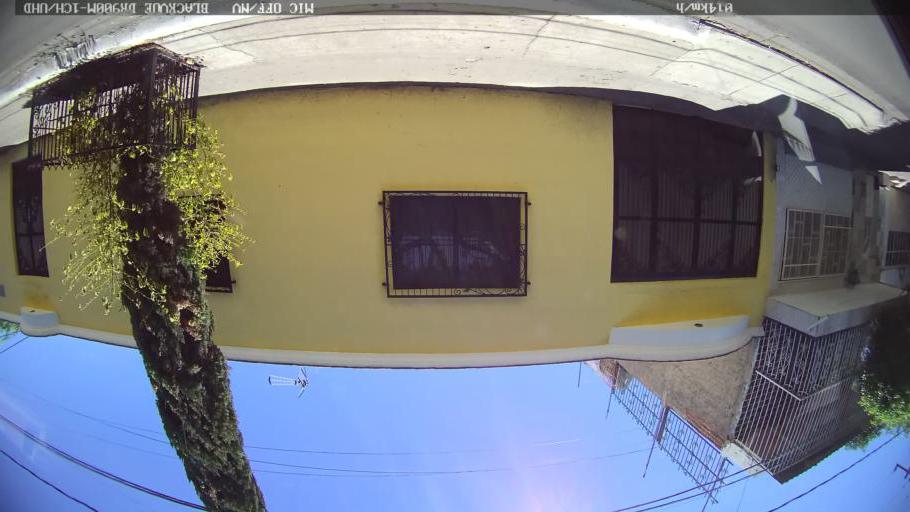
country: MX
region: Jalisco
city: Tlaquepaque
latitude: 20.6718
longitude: -103.2725
